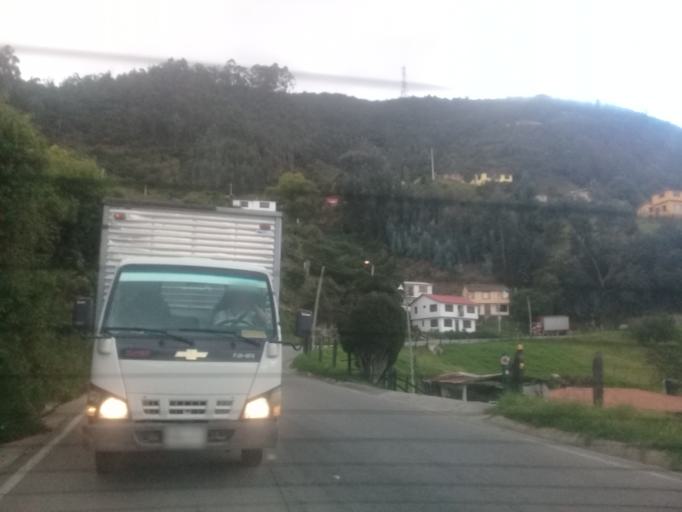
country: CO
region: Cundinamarca
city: Tabio
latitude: 4.9355
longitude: -74.1075
